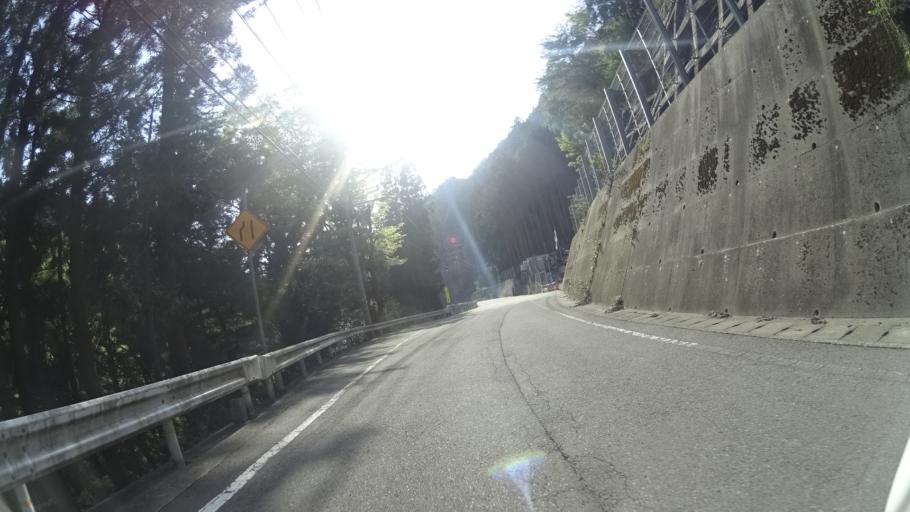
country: JP
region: Tokushima
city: Ikedacho
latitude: 33.8681
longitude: 133.9696
